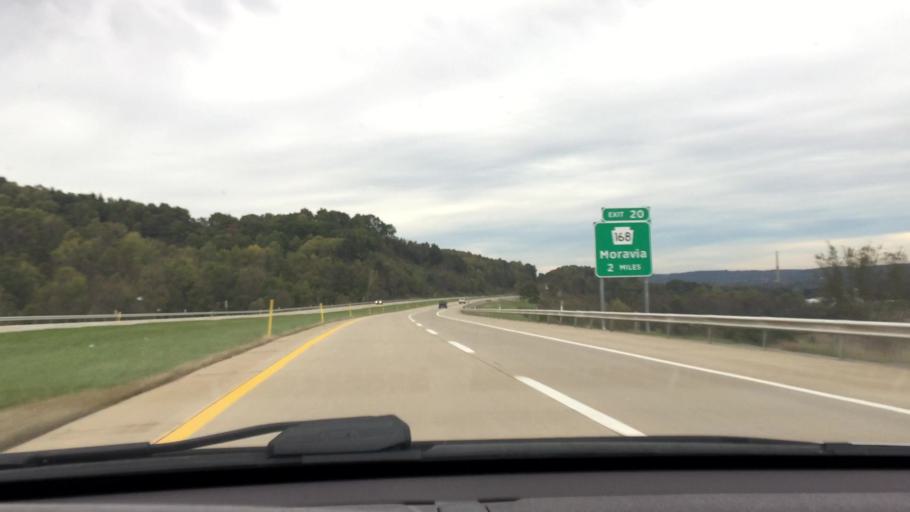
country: US
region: Pennsylvania
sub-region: Lawrence County
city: New Beaver
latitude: 40.8822
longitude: -80.3709
